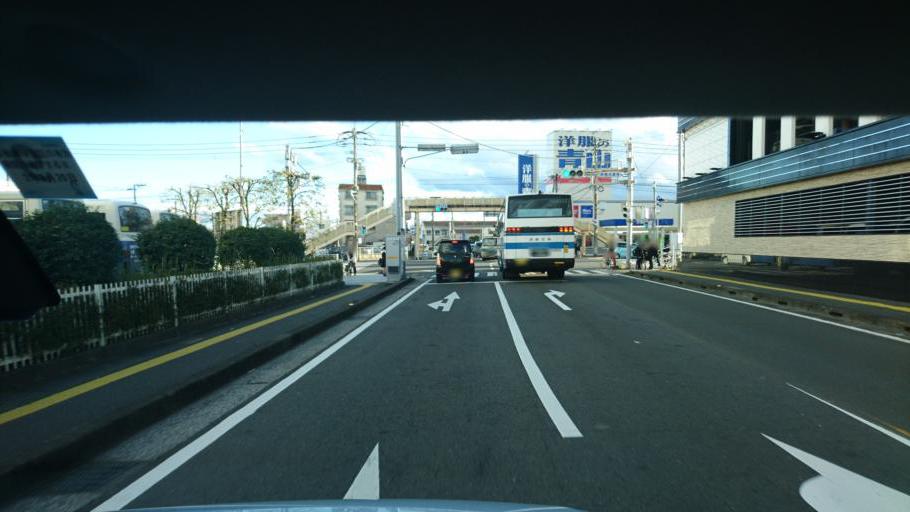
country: JP
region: Miyazaki
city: Miyazaki-shi
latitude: 31.8945
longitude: 131.4189
